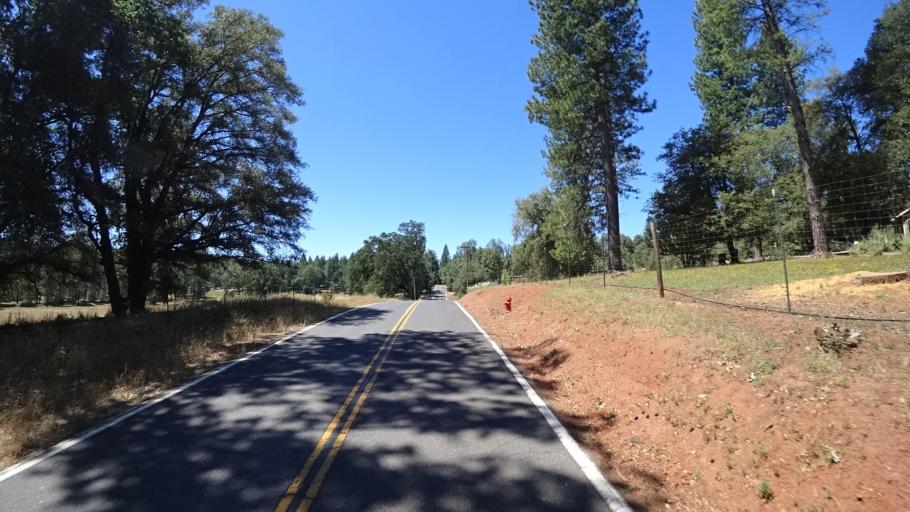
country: US
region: California
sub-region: Amador County
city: Pioneer
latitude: 38.3491
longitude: -120.5621
